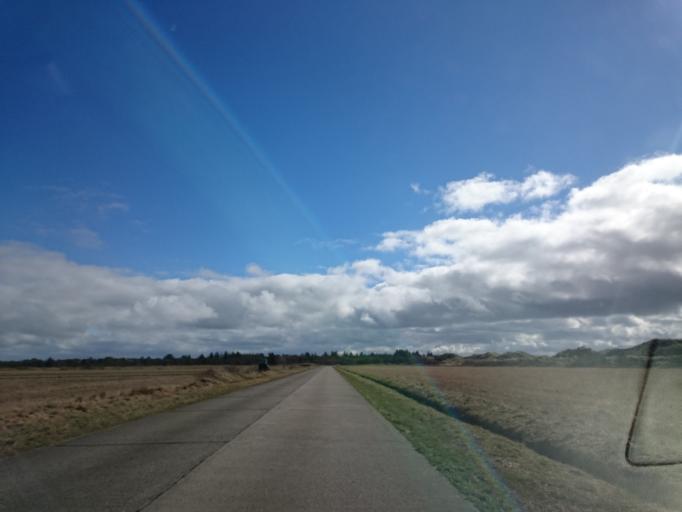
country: DK
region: North Denmark
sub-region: Frederikshavn Kommune
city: Skagen
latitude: 57.6588
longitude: 10.4067
